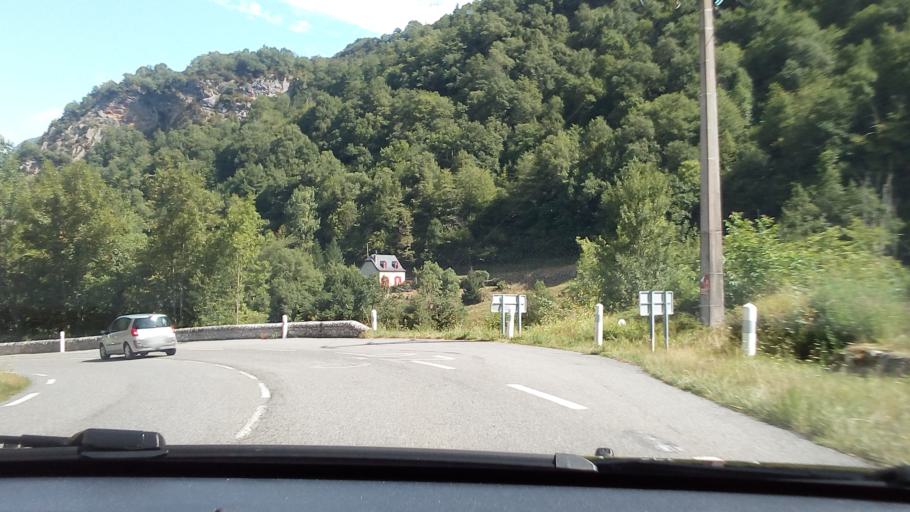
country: FR
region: Aquitaine
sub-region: Departement des Pyrenees-Atlantiques
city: Laruns
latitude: 42.8942
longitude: -0.5647
